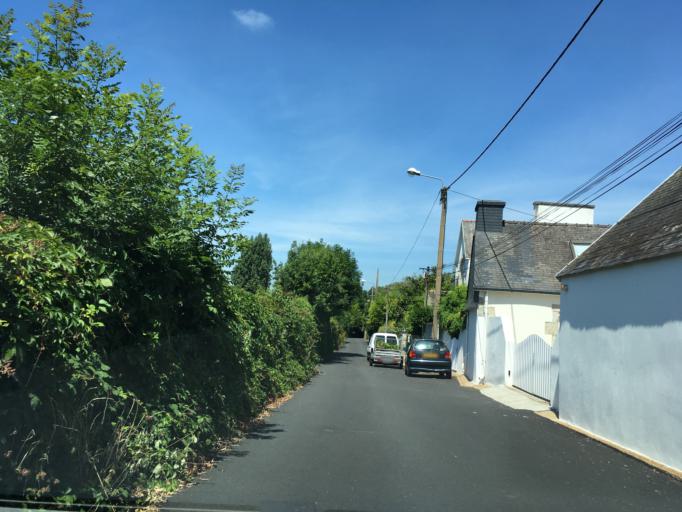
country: FR
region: Brittany
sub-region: Departement du Finistere
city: Quimper
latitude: 48.0024
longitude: -4.1051
